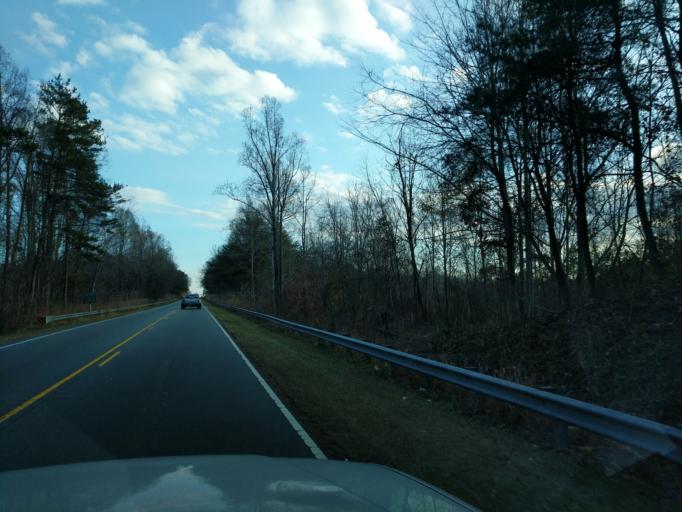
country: US
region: North Carolina
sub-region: Rutherford County
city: Rutherfordton
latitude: 35.4155
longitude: -81.9739
